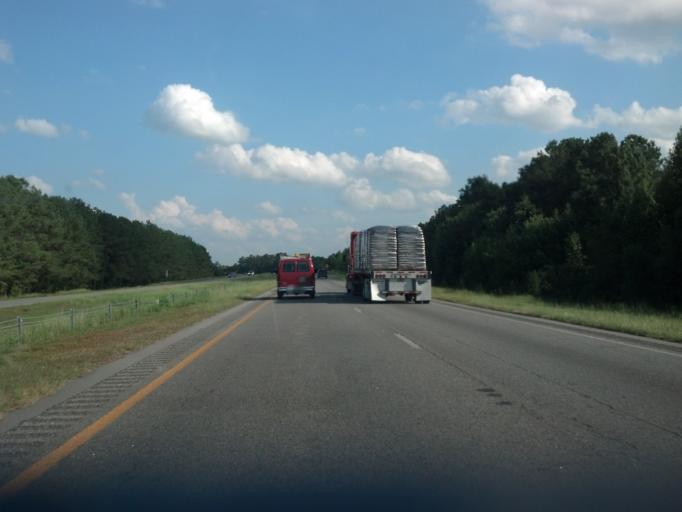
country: US
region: North Carolina
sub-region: Edgecombe County
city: Tarboro
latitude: 35.9024
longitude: -77.6407
